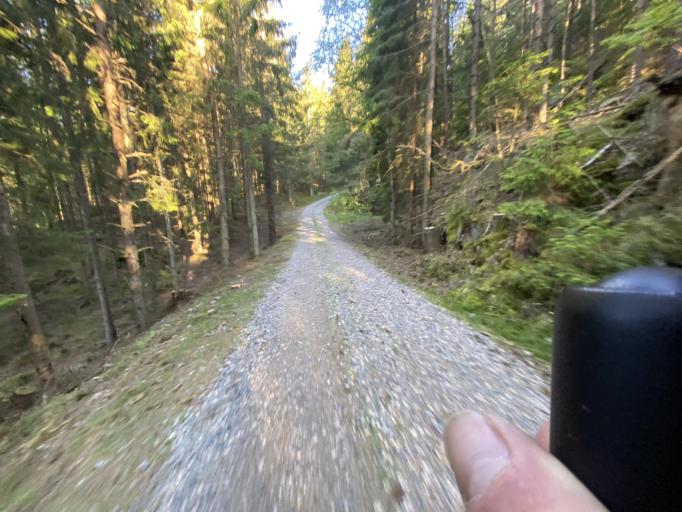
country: SE
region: Vaestra Goetaland
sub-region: Alingsas Kommun
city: Ingared
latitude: 57.9763
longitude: 12.3813
